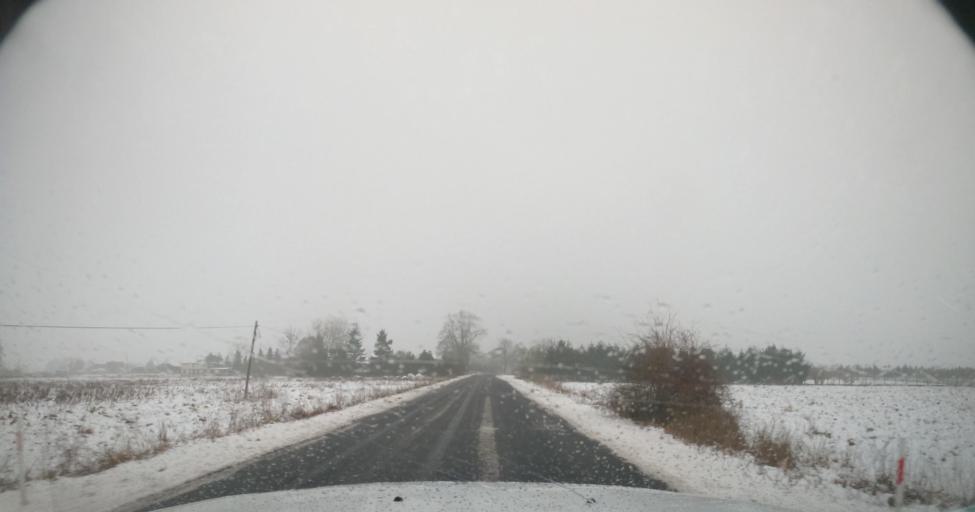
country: PL
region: West Pomeranian Voivodeship
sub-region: Powiat goleniowski
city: Goleniow
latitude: 53.5769
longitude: 14.7318
